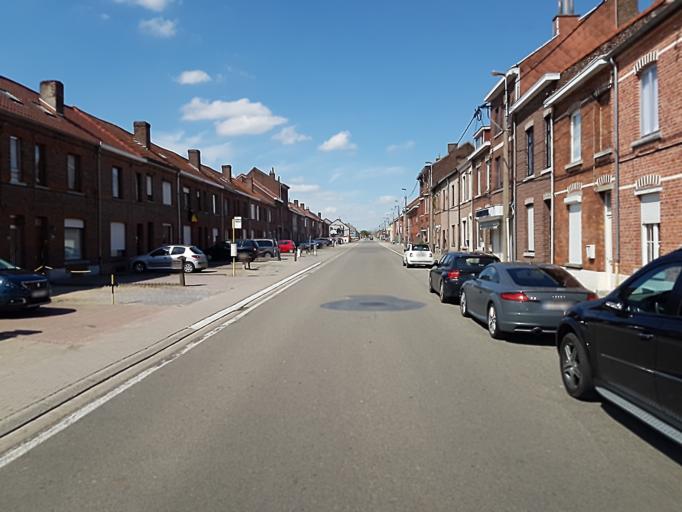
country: BE
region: Flanders
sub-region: Provincie Vlaams-Brabant
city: Tienen
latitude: 50.8162
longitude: 4.9268
